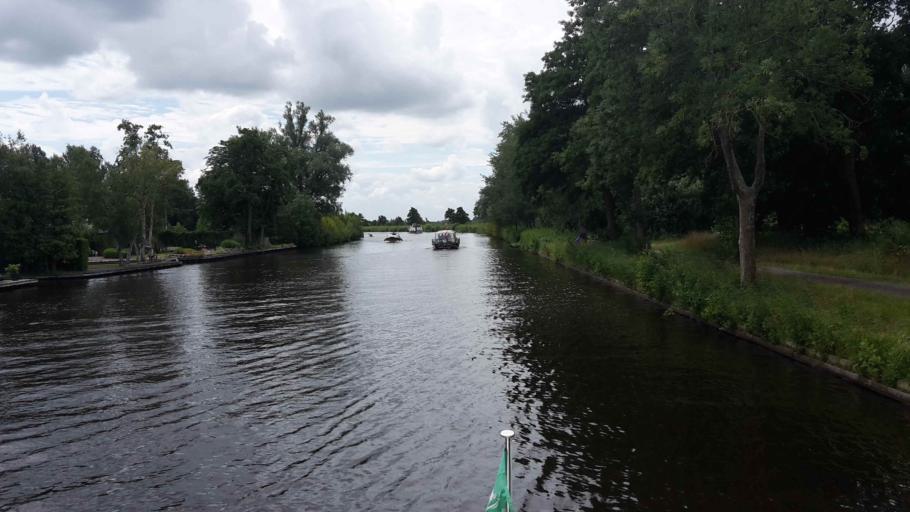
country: NL
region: Overijssel
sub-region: Gemeente Steenwijkerland
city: Giethoorn
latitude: 52.7102
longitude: 6.0736
